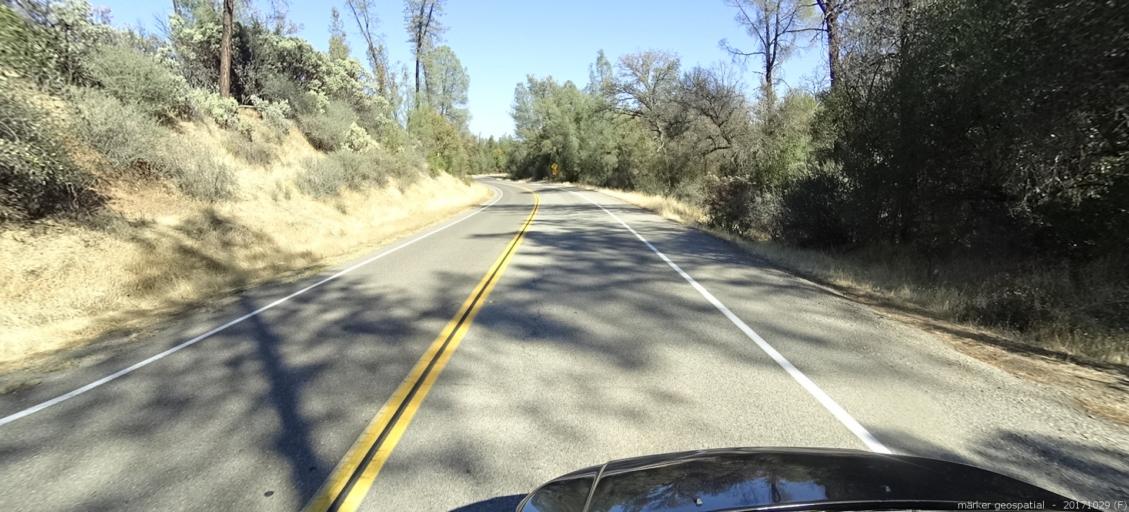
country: US
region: California
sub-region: Shasta County
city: Shasta
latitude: 40.4969
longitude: -122.4616
